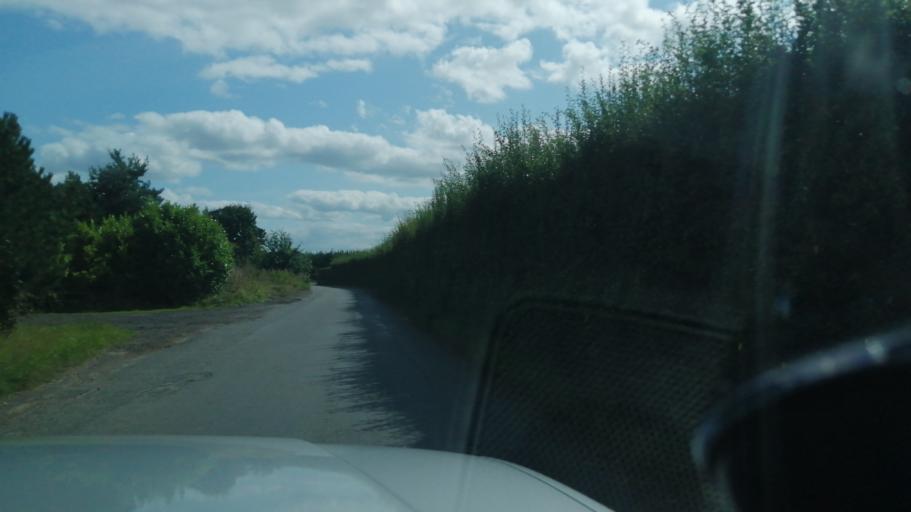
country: GB
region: England
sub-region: Herefordshire
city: Madley
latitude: 52.0224
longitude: -2.8585
